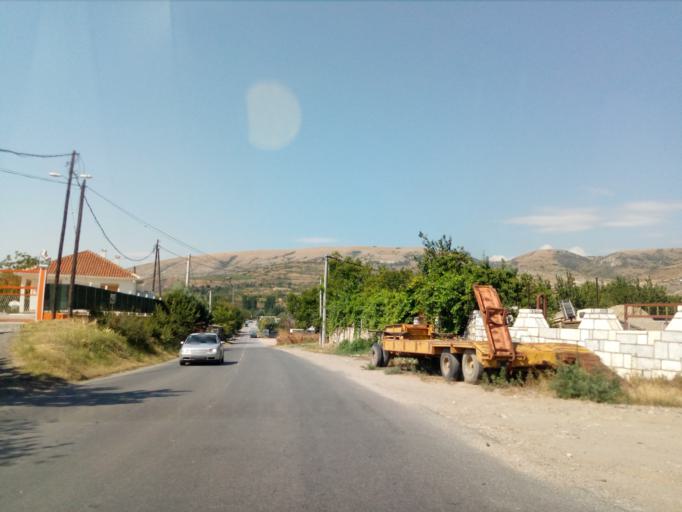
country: MK
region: Veles
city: Veles
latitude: 41.7460
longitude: 21.7665
